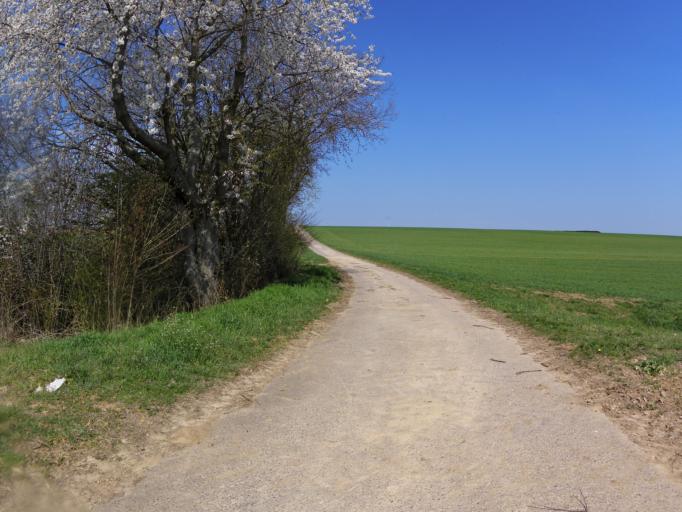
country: DE
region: Bavaria
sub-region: Regierungsbezirk Unterfranken
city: Mainstockheim
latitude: 49.8112
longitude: 10.1126
